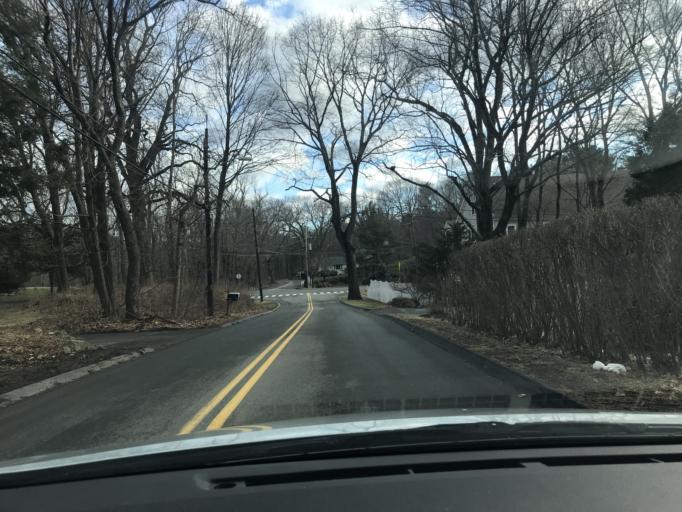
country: US
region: Massachusetts
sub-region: Middlesex County
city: Lexington
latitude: 42.4664
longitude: -71.2147
